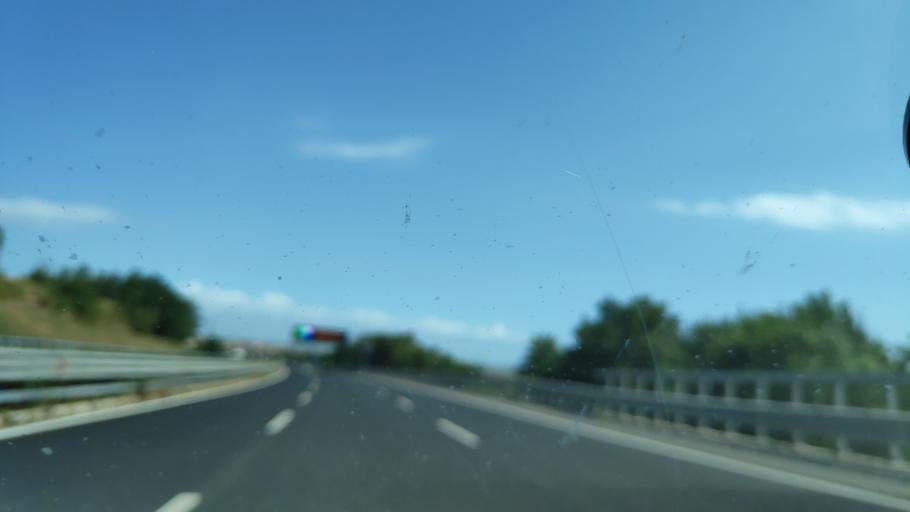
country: IT
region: Campania
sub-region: Provincia di Salerno
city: Fuorni
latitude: 40.6616
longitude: 14.8595
